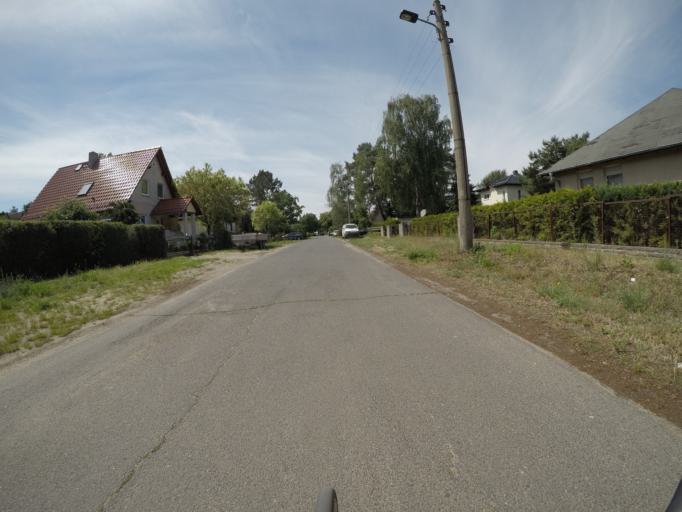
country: DE
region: Berlin
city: Mahlsdorf
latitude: 52.4864
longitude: 13.6177
